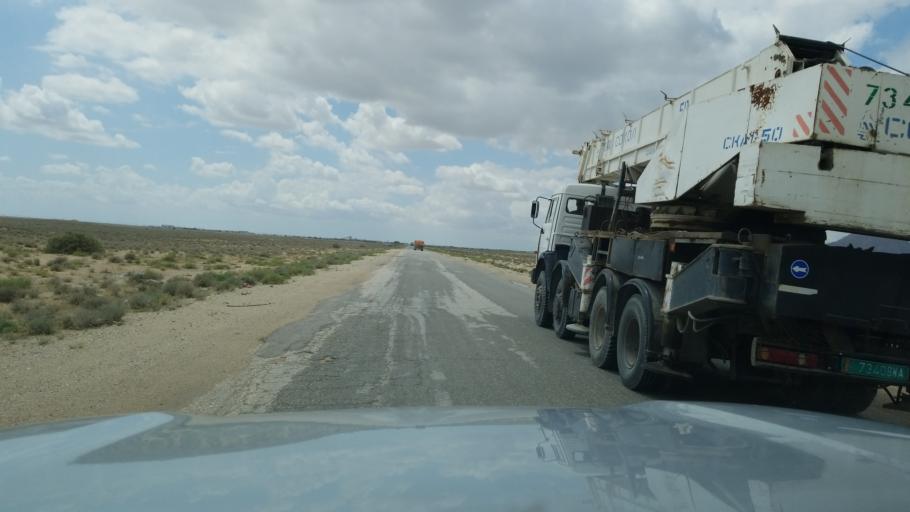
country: TM
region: Balkan
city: Balkanabat
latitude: 39.4838
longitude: 54.4346
